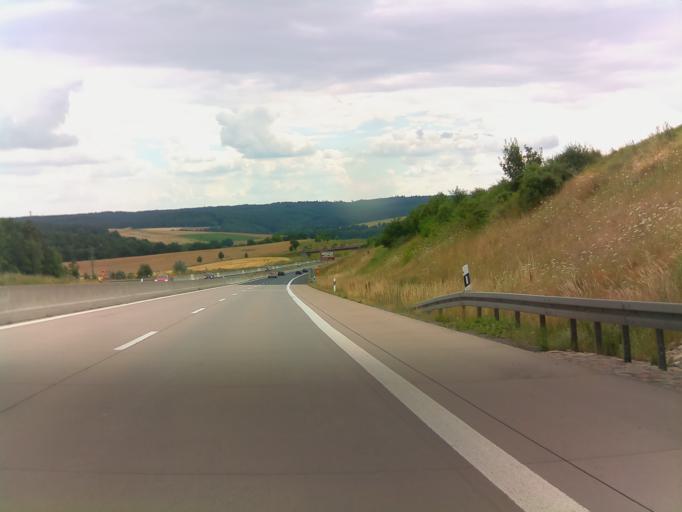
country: DE
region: Bavaria
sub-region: Regierungsbezirk Unterfranken
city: Hollstadt
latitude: 50.3560
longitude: 10.3171
